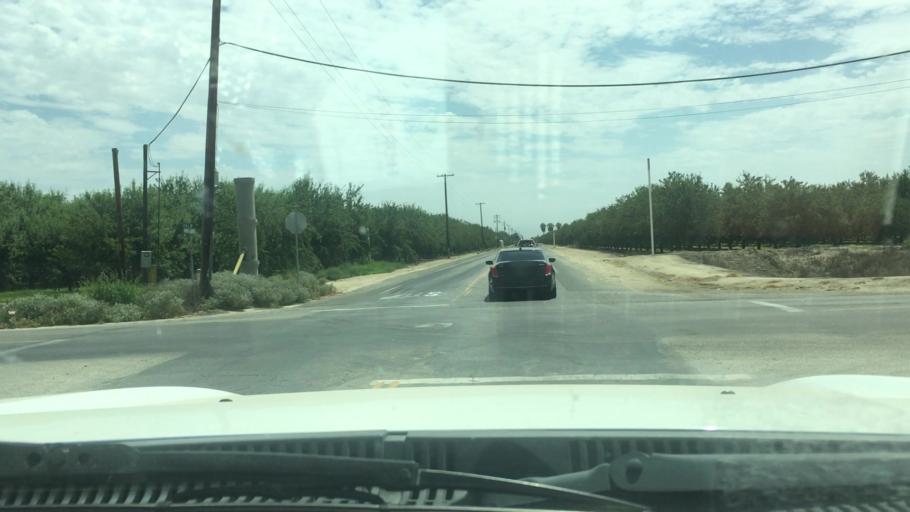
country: US
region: California
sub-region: Kern County
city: Wasco
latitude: 35.5580
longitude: -119.3497
